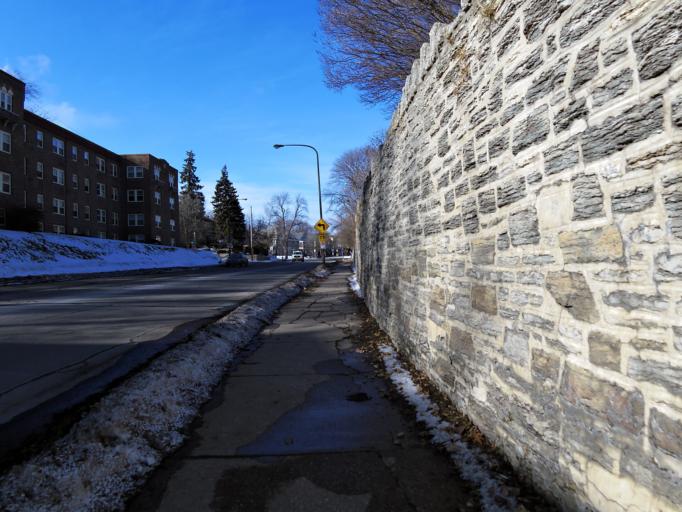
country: US
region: Minnesota
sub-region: Ramsey County
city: Saint Paul
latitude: 44.9388
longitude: -93.1224
